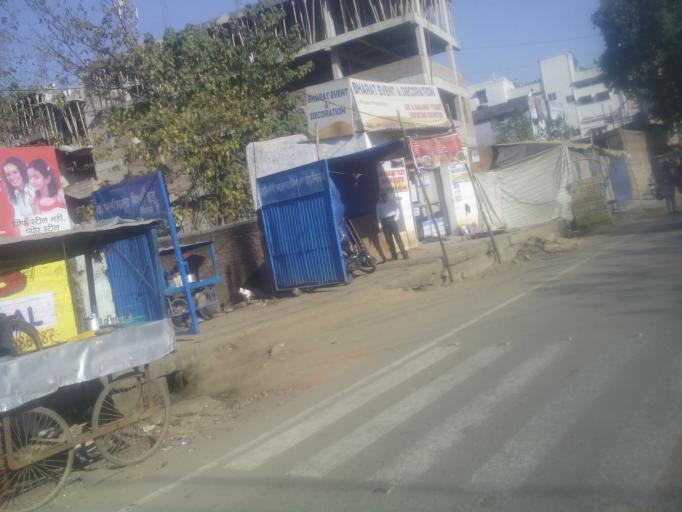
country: IN
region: Jharkhand
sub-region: Ranchi
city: Ranchi
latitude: 23.3656
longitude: 85.3434
